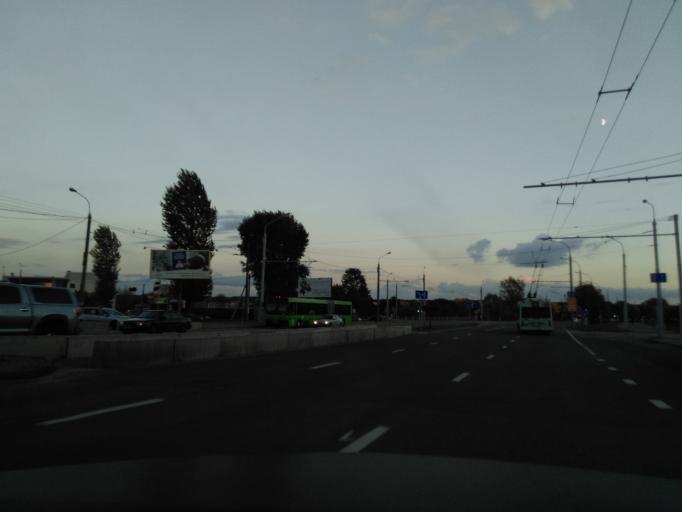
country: BY
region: Minsk
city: Minsk
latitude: 53.9295
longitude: 27.6393
